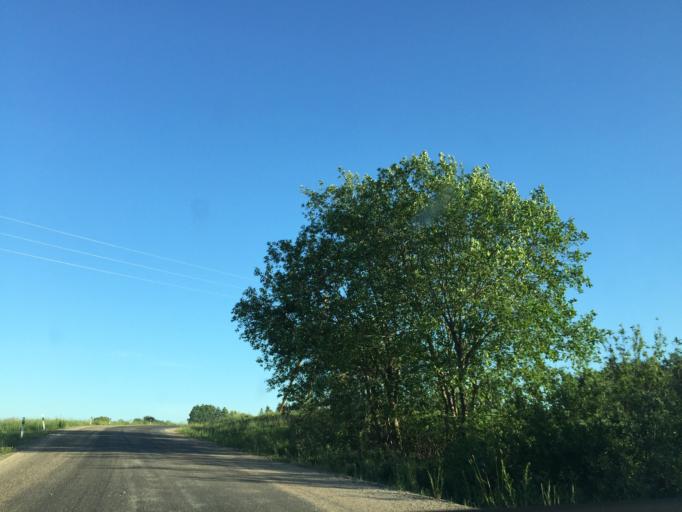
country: LV
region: Broceni
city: Broceni
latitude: 56.7638
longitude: 22.5245
